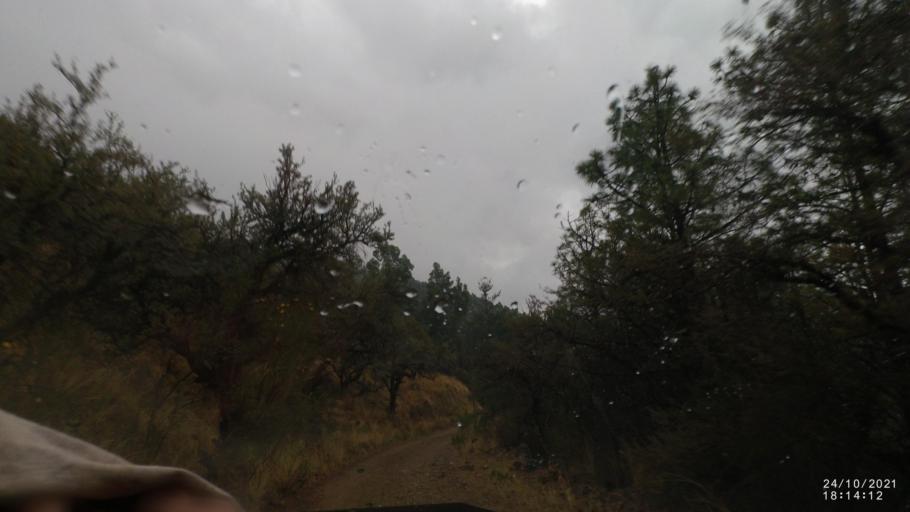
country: BO
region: Cochabamba
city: Cochabamba
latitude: -17.3287
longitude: -66.1369
